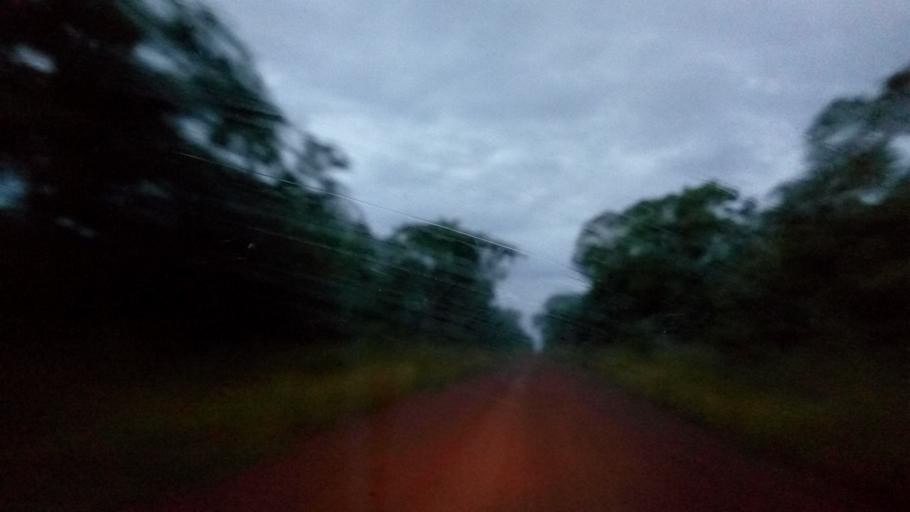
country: ZM
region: Luapula
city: Nchelenge
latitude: -9.7951
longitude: 28.1523
